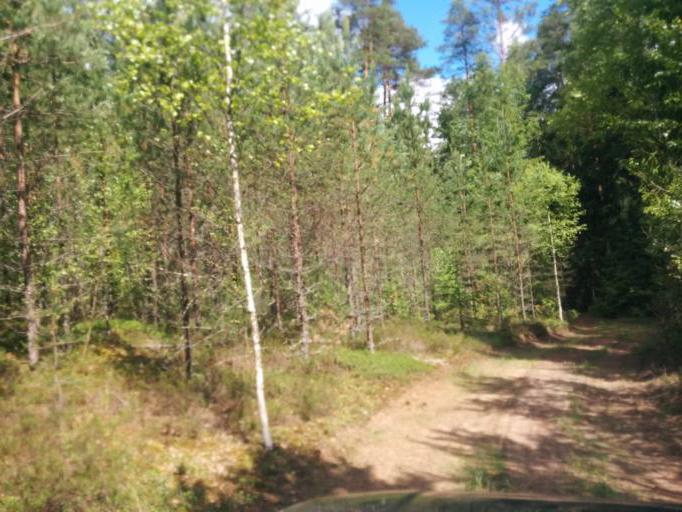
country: LV
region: Vilaka
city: Vilaka
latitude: 57.3337
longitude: 27.6923
